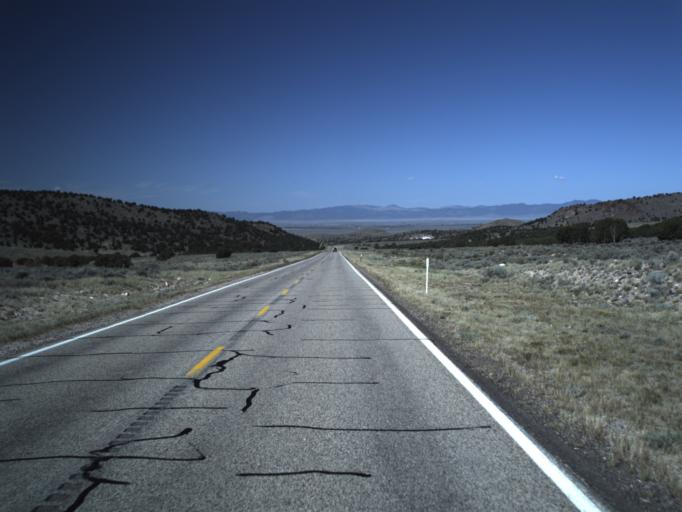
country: US
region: Utah
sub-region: Washington County
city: Enterprise
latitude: 37.6674
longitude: -113.4781
